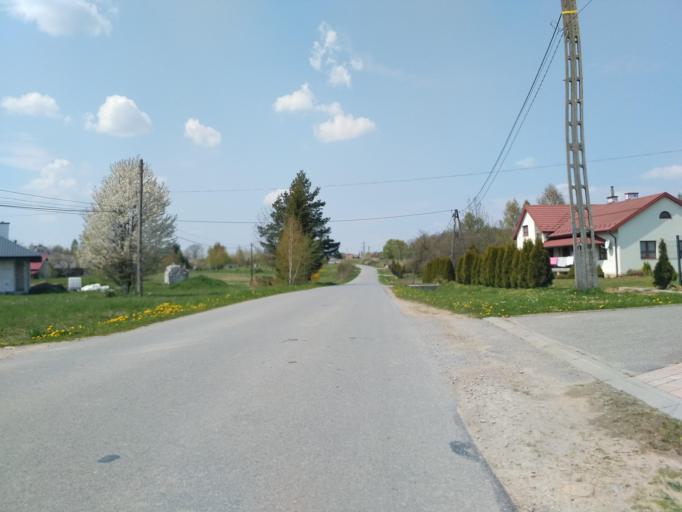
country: PL
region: Subcarpathian Voivodeship
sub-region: Powiat jasielski
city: Osiek Jasielski
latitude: 49.6712
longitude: 21.5329
